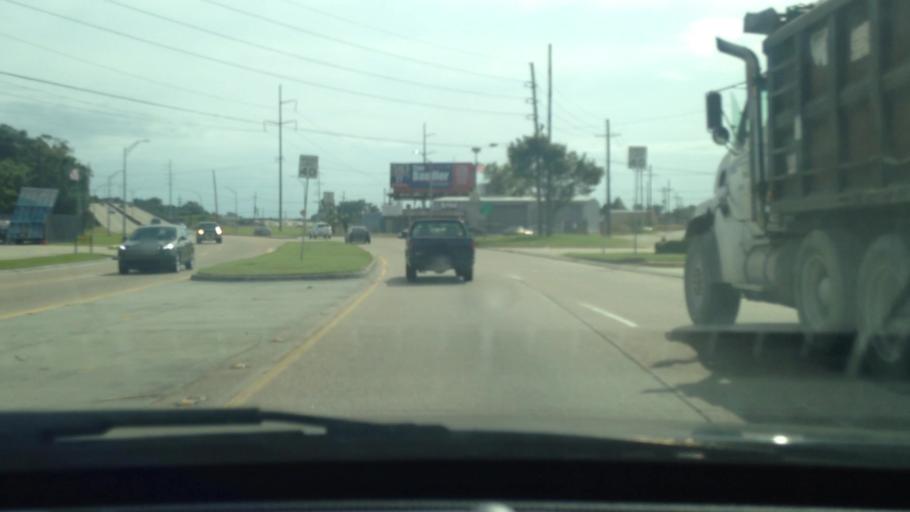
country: US
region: Louisiana
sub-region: Jefferson Parish
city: River Ridge
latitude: 29.9763
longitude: -90.2103
